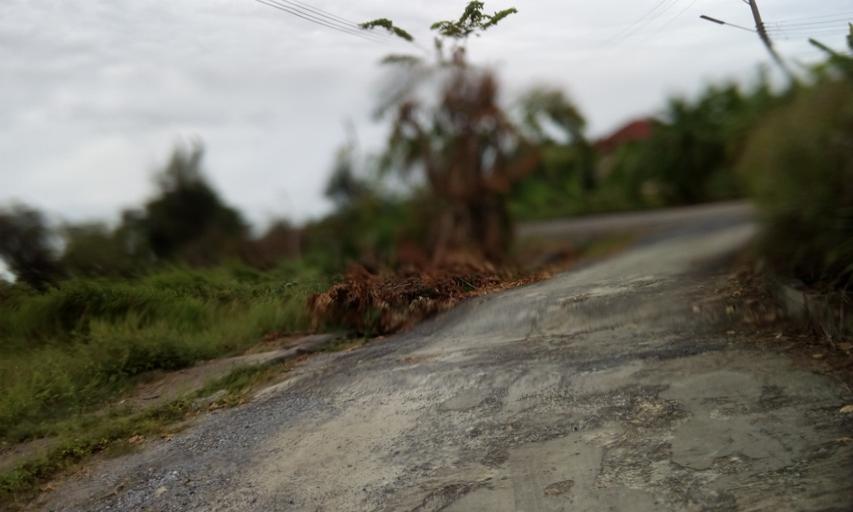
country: TH
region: Pathum Thani
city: Nong Suea
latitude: 14.0621
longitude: 100.8781
